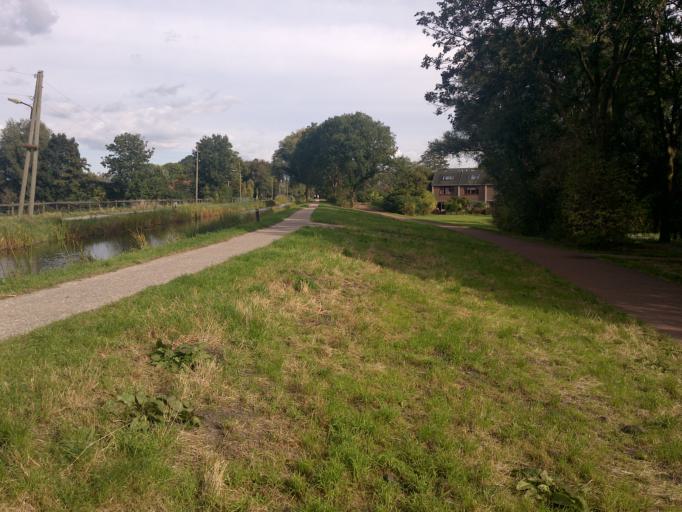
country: NL
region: South Holland
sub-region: Gemeente Zoetermeer
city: Zoetermeer
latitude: 52.0704
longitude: 4.4699
